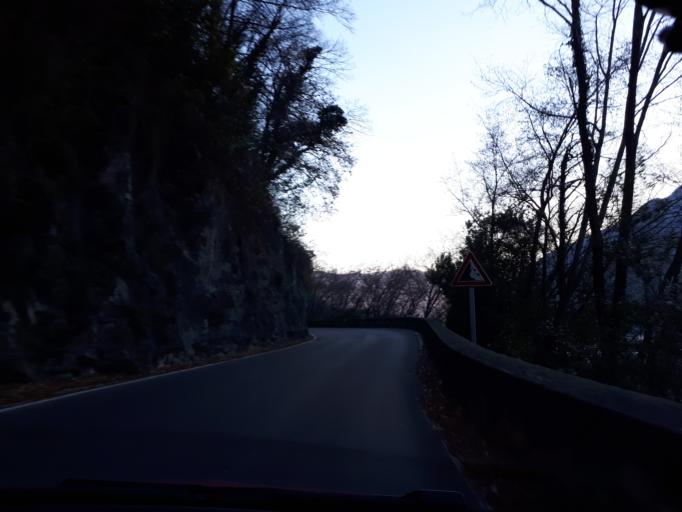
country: IT
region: Lombardy
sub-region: Provincia di Como
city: Nesso
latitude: 45.9281
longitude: 9.1504
